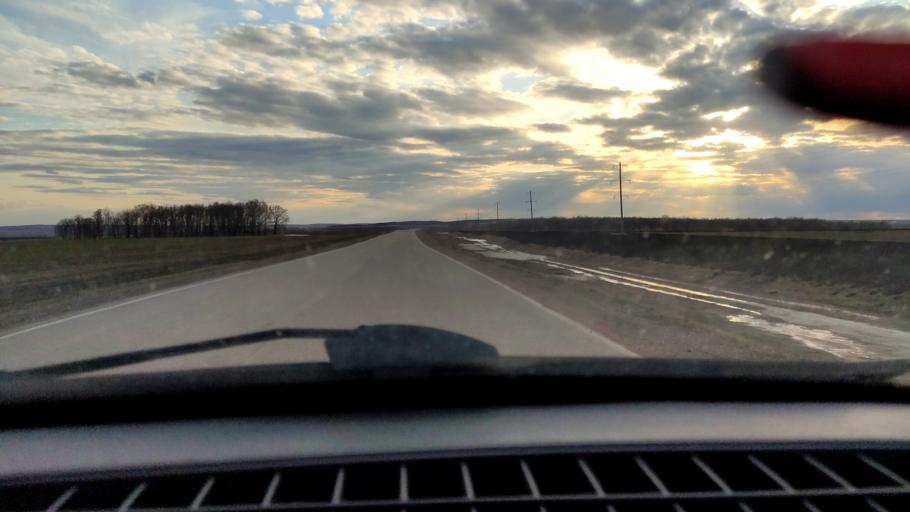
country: RU
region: Bashkortostan
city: Tolbazy
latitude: 53.9933
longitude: 55.8365
